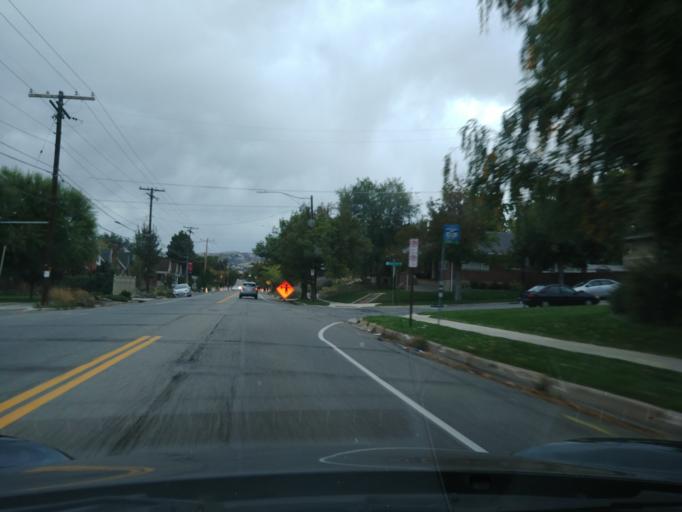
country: US
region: Utah
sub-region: Salt Lake County
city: Willard
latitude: 40.7342
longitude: -111.8539
